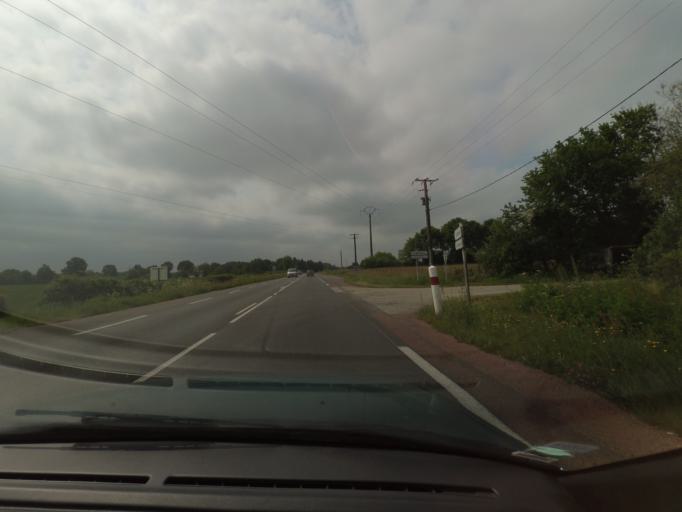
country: FR
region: Pays de la Loire
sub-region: Departement de la Vendee
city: La Boissiere-des-Landes
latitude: 46.5750
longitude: -1.4503
